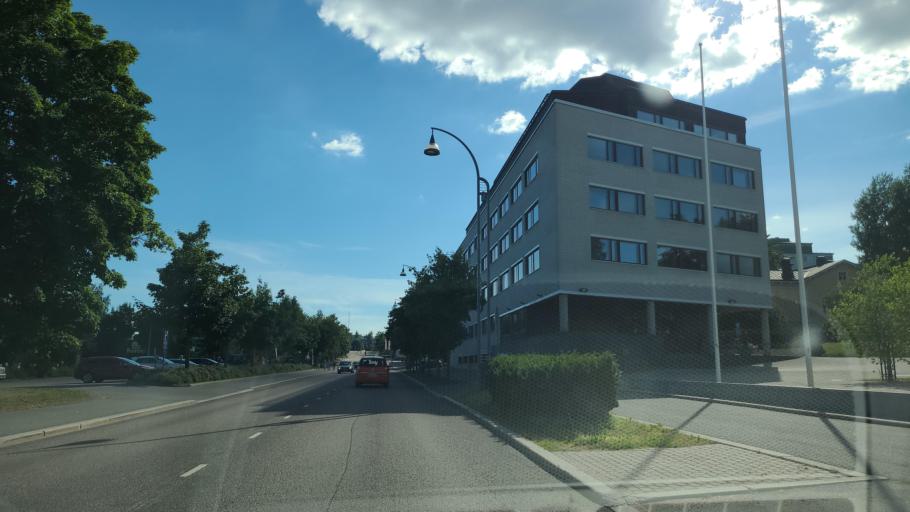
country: FI
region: Central Finland
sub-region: Jyvaeskylae
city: Jyvaeskylae
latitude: 62.2392
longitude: 25.7487
